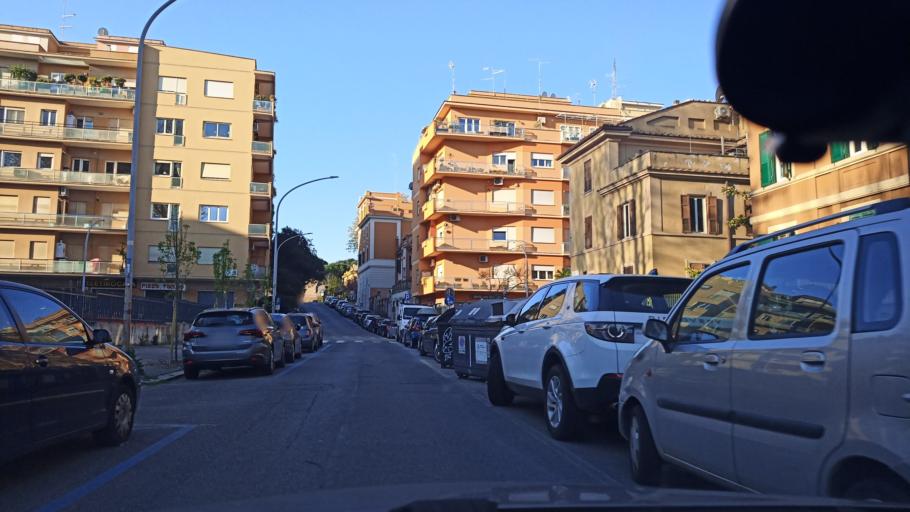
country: IT
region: Latium
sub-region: Citta metropolitana di Roma Capitale
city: Rome
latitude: 41.8771
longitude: 12.5044
